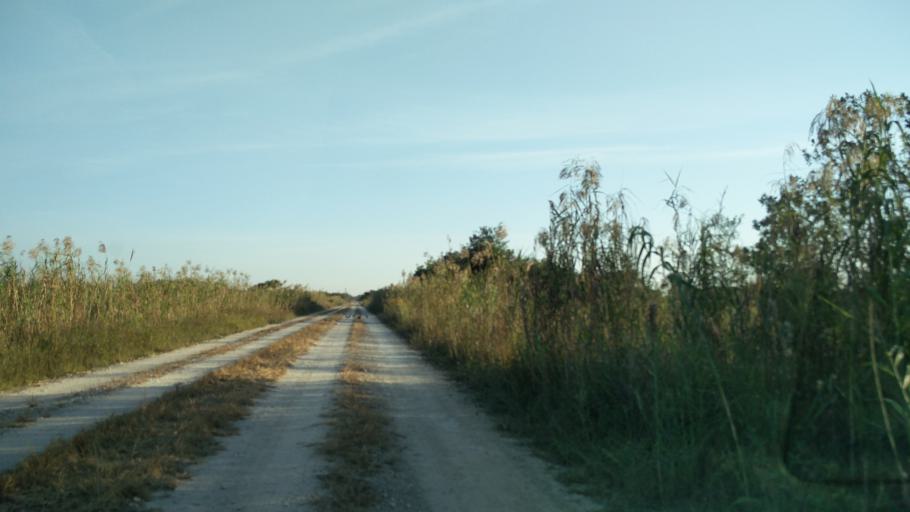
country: US
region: Florida
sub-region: Collier County
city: Lely Resort
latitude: 25.9672
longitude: -81.3664
